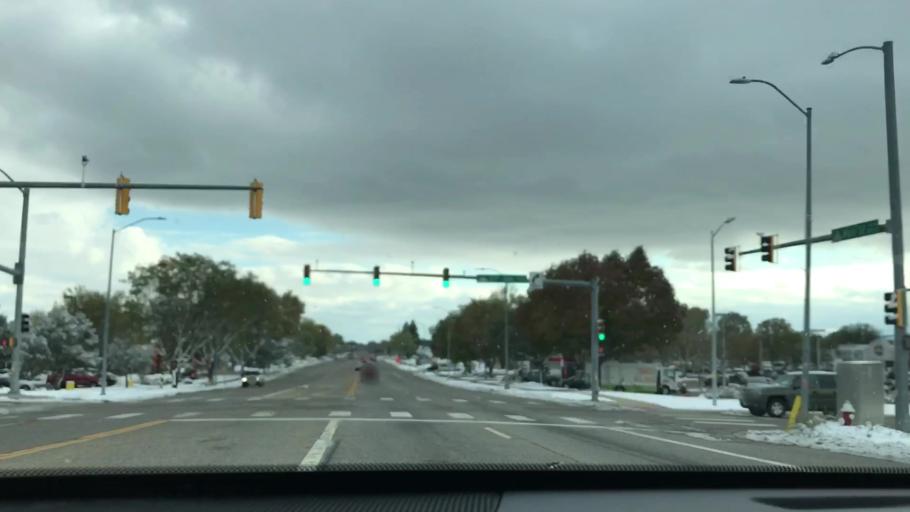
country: US
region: Colorado
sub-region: Boulder County
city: Longmont
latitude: 40.1998
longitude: -105.1025
